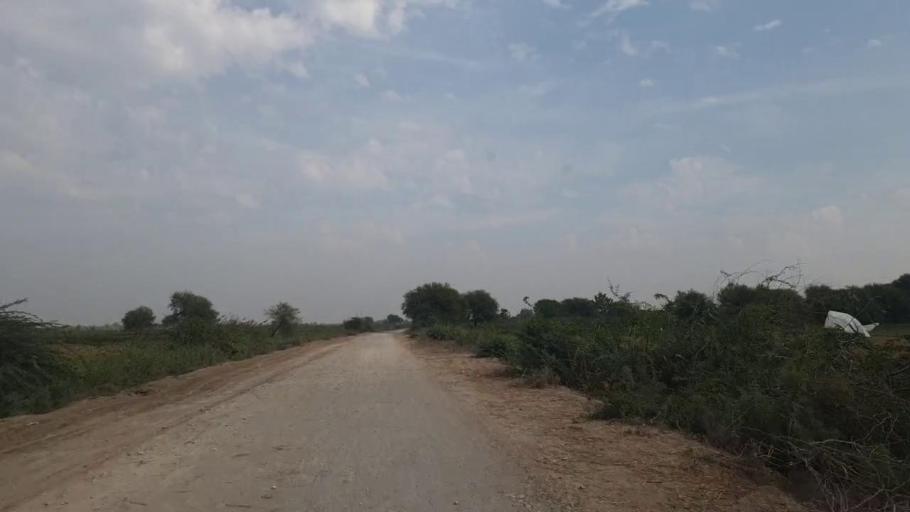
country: PK
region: Sindh
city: Rajo Khanani
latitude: 24.9577
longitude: 68.9940
